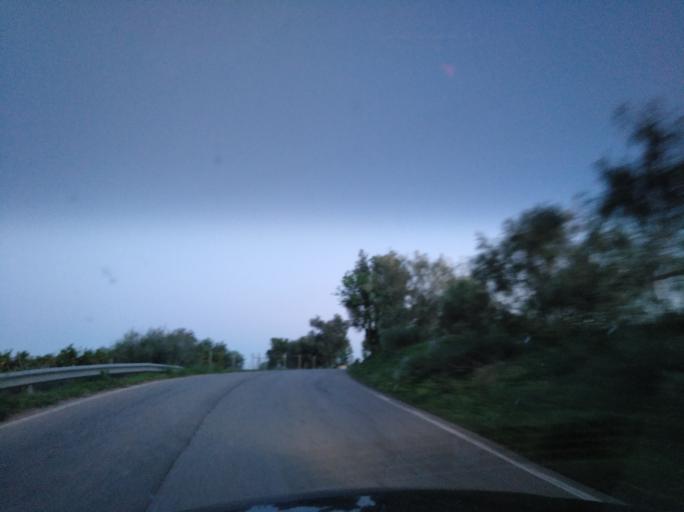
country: PT
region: Faro
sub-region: Vila Real de Santo Antonio
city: Monte Gordo
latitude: 37.1941
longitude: -7.5148
